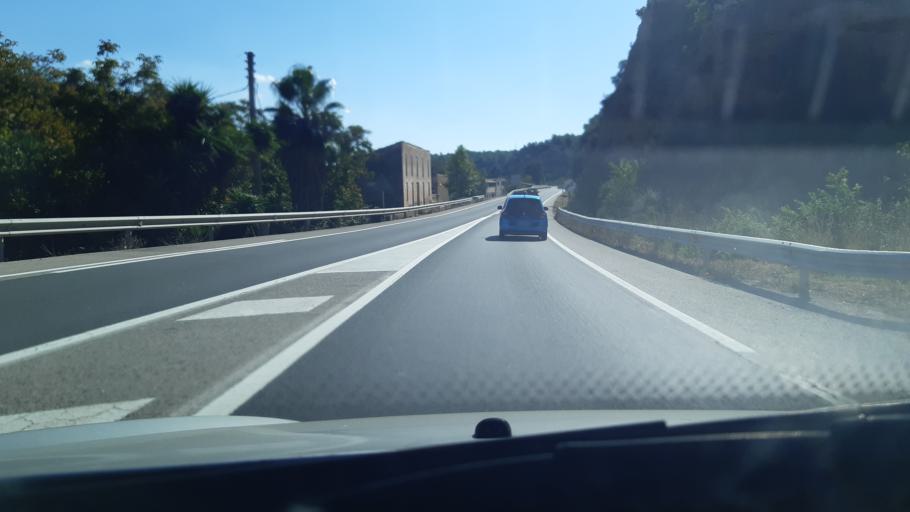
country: ES
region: Catalonia
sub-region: Provincia de Tarragona
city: Tivenys
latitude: 40.8756
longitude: 0.5008
